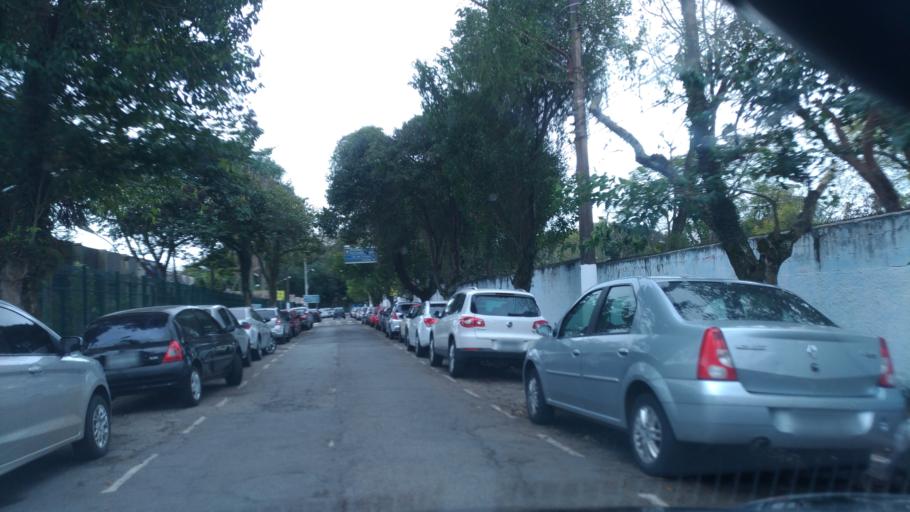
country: BR
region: Sao Paulo
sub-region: Sao Bernardo Do Campo
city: Sao Bernardo do Campo
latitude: -23.6894
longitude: -46.5575
